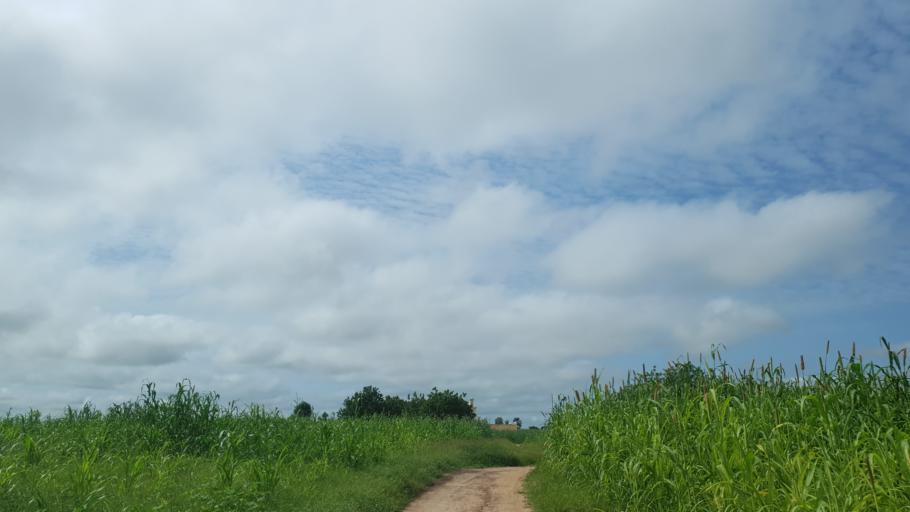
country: ML
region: Segou
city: Baroueli
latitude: 13.4867
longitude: -6.8961
